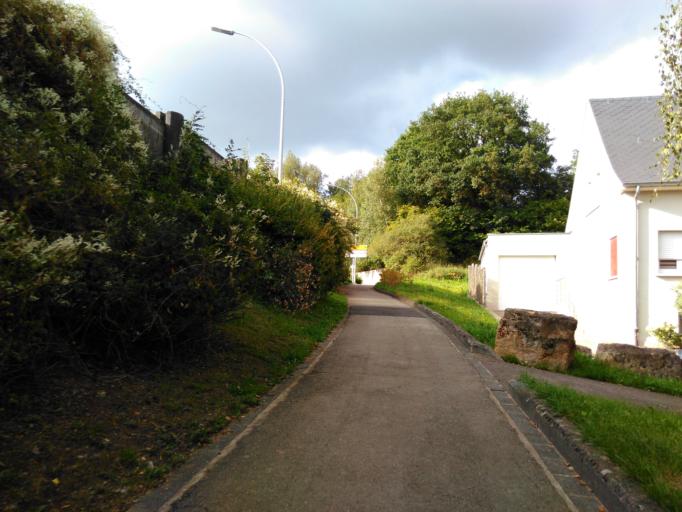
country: LU
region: Luxembourg
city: Belvaux
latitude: 49.5133
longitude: 5.9294
